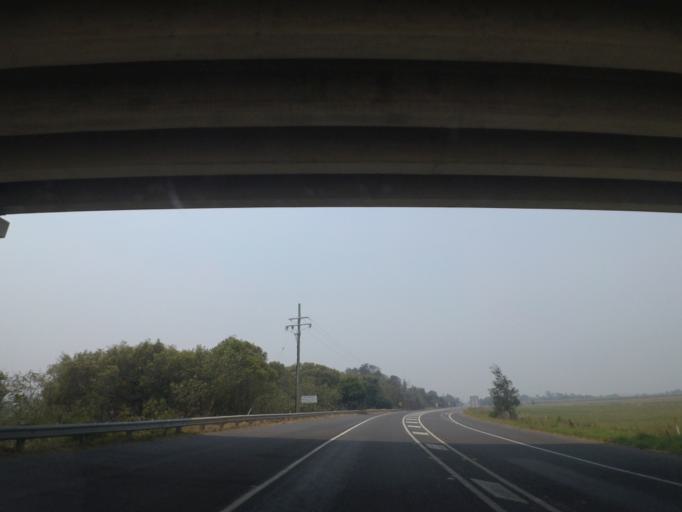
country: AU
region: New South Wales
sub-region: Richmond Valley
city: Evans Head
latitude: -28.9995
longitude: 153.4408
